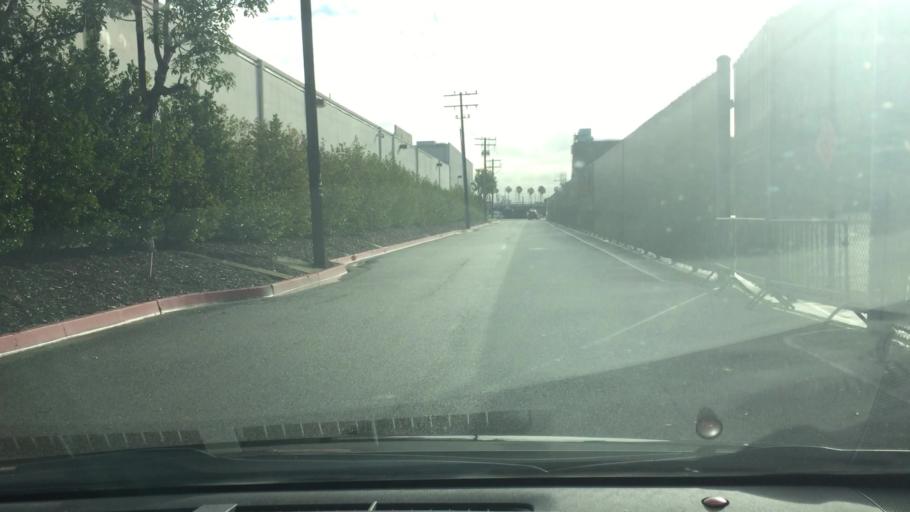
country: US
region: California
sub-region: Orange County
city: Anaheim
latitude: 33.8088
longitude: -117.9119
